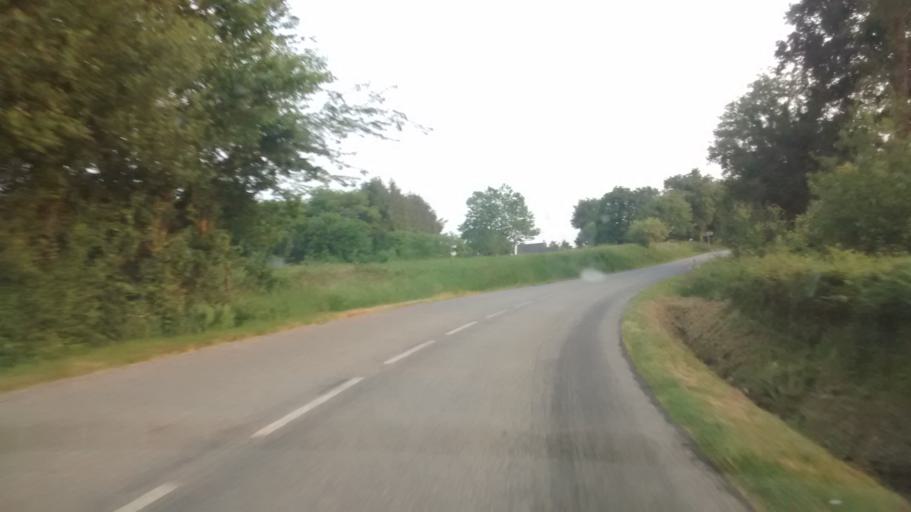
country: FR
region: Brittany
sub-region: Departement du Morbihan
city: Beignon
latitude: 47.9722
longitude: -2.1505
